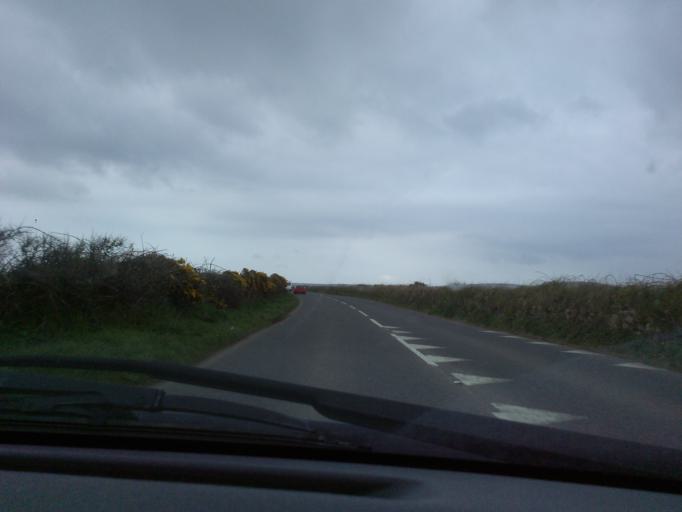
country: GB
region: England
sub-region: Cornwall
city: Sennen
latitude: 50.0805
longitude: -5.6815
